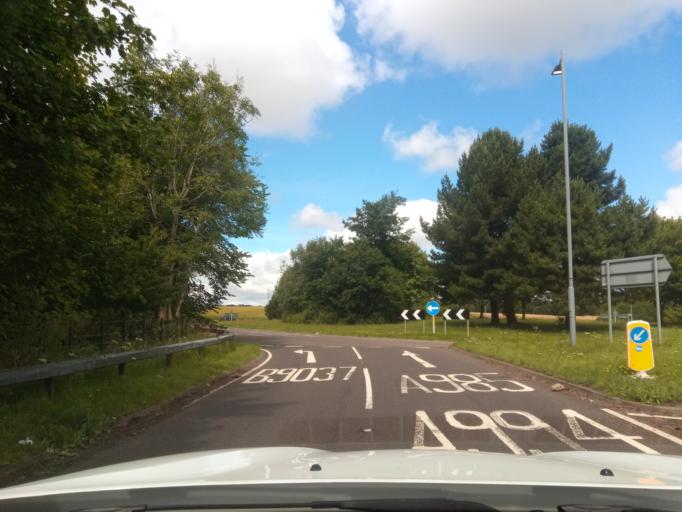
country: GB
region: Scotland
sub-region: Fife
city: Cairneyhill
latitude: 56.0591
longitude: -3.5445
